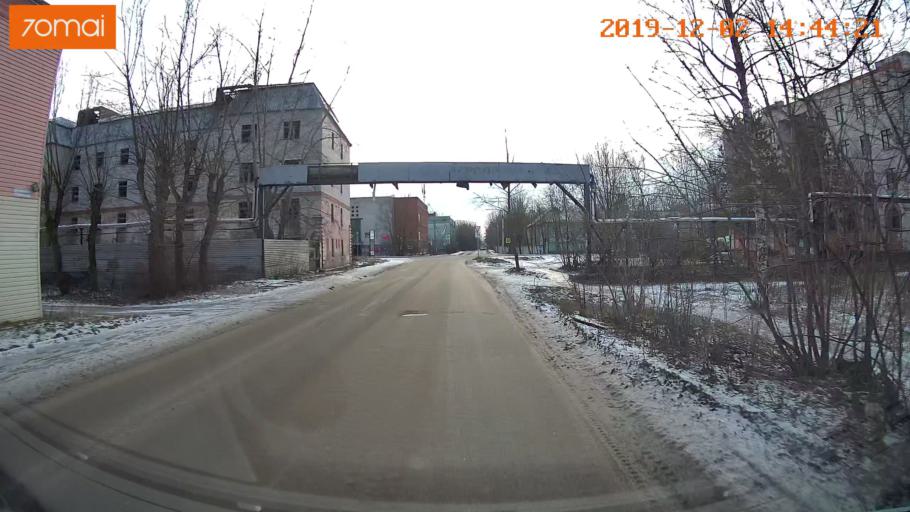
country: RU
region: Ivanovo
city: Bogorodskoye
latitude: 56.9899
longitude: 41.0378
